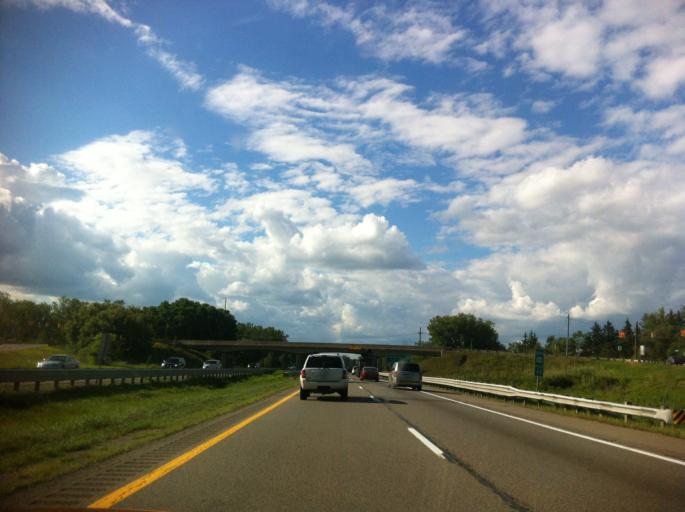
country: US
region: Michigan
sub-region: Livingston County
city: Whitmore Lake
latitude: 42.3781
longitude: -83.7560
